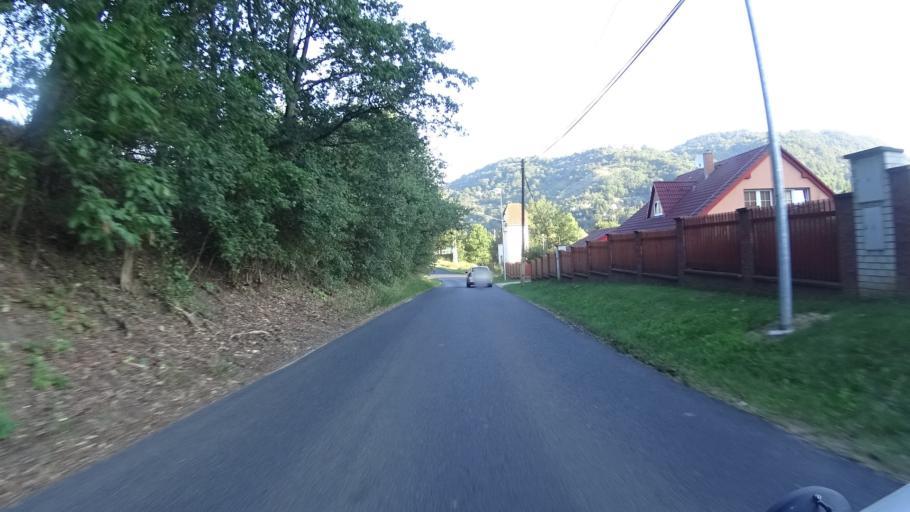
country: CZ
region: Ustecky
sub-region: Okres Usti nad Labem
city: Usti nad Labem
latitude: 50.5922
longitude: 14.0675
